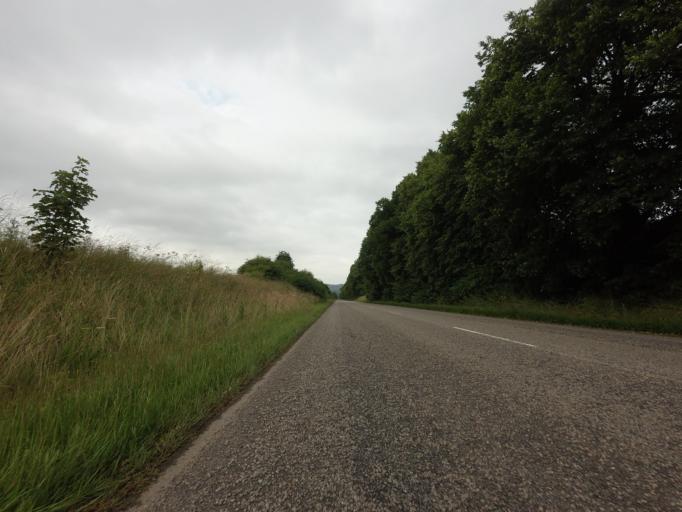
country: GB
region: Scotland
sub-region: Highland
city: Alness
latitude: 57.9118
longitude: -4.3756
